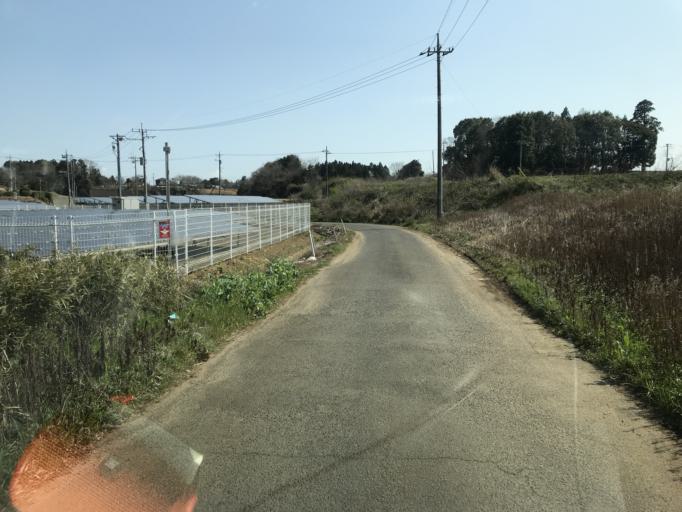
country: JP
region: Chiba
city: Sawara
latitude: 35.8333
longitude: 140.5204
